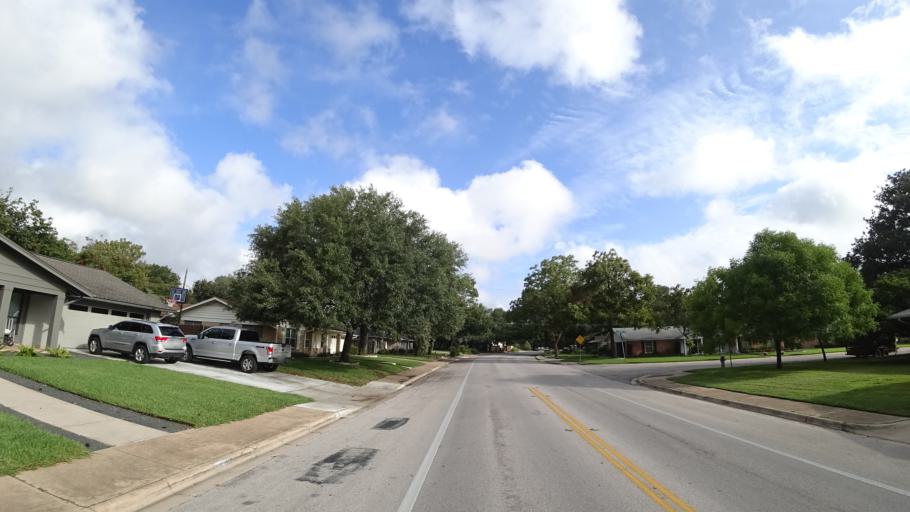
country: US
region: Texas
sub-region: Travis County
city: West Lake Hills
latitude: 30.3545
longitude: -97.7405
